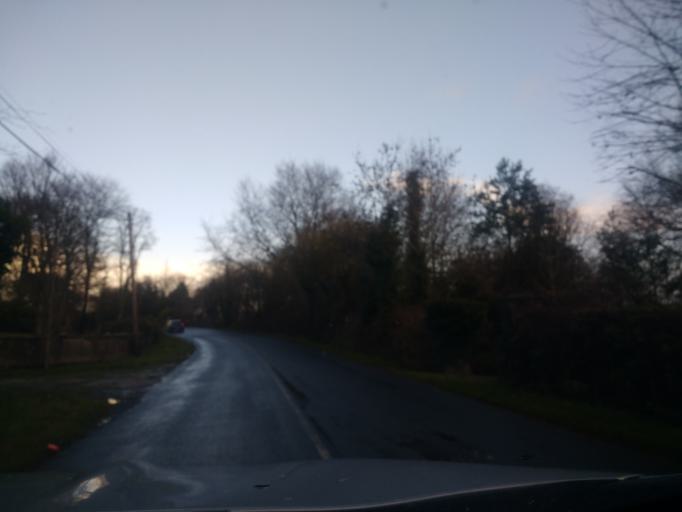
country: IE
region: Ulster
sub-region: County Donegal
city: Ramelton
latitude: 55.0463
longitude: -7.6435
